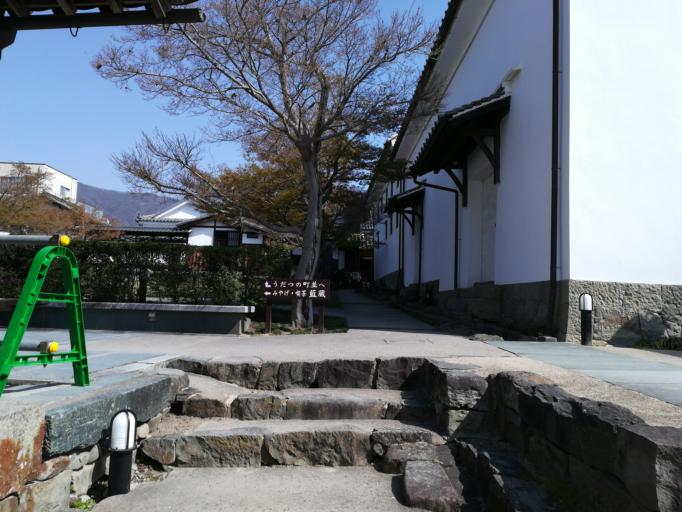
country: JP
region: Tokushima
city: Wakimachi
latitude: 34.0675
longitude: 134.1466
